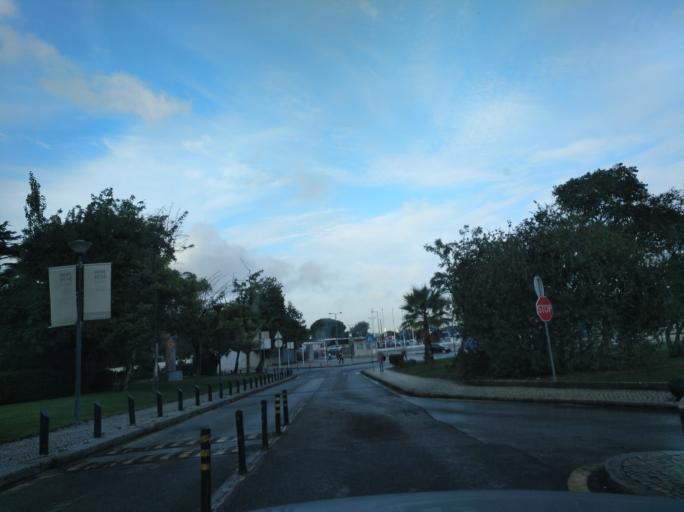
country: PT
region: Lisbon
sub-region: Odivelas
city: Olival do Basto
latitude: 38.7493
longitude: -9.1616
